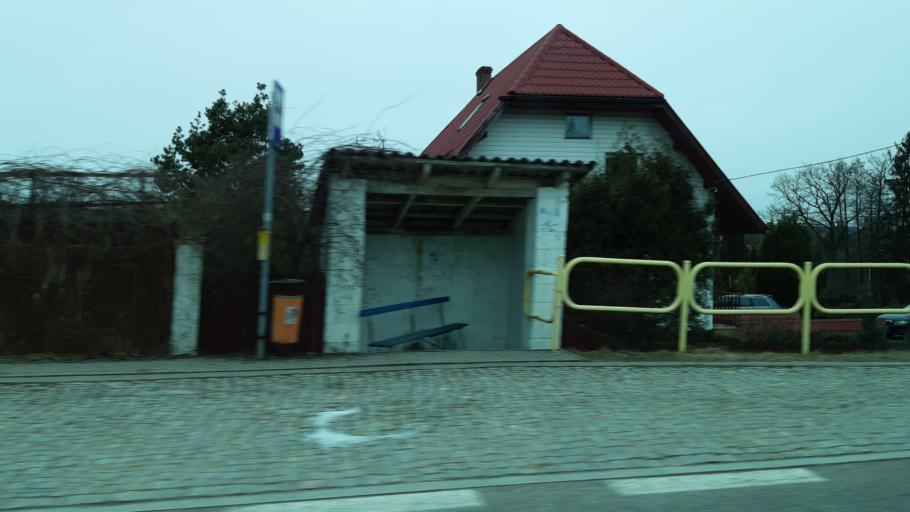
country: PL
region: Podlasie
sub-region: Suwalki
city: Suwalki
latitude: 54.3150
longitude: 22.9614
